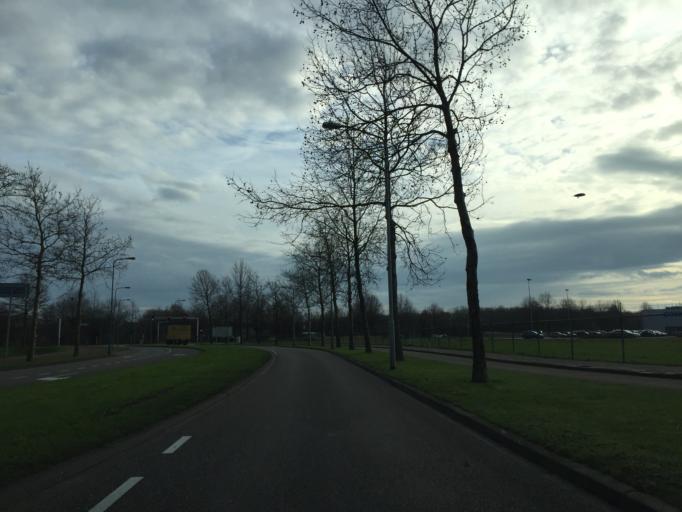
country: NL
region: North Brabant
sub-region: Gemeente 's-Hertogenbosch
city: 's-Hertogenbosch
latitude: 51.7218
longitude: 5.2925
